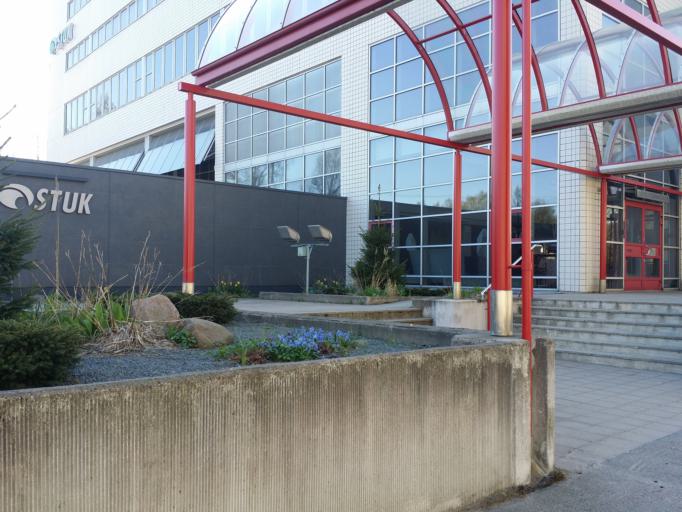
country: FI
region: Uusimaa
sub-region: Helsinki
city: Helsinki
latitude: 60.1943
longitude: 25.0296
